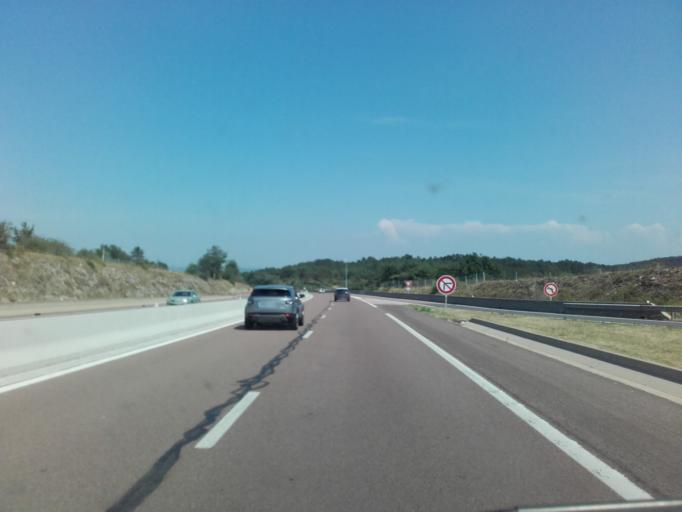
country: FR
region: Bourgogne
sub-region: Departement de la Cote-d'Or
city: Savigny-les-Beaune
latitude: 47.0578
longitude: 4.7956
